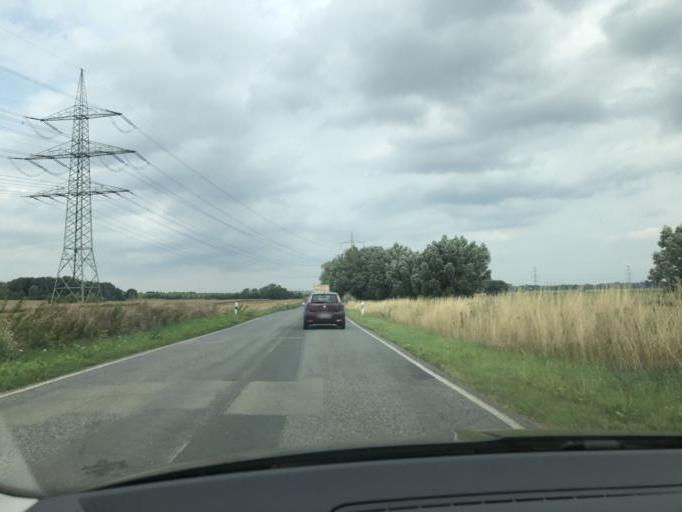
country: DE
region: Mecklenburg-Vorpommern
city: Klein Rogahn
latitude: 53.5878
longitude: 11.3349
